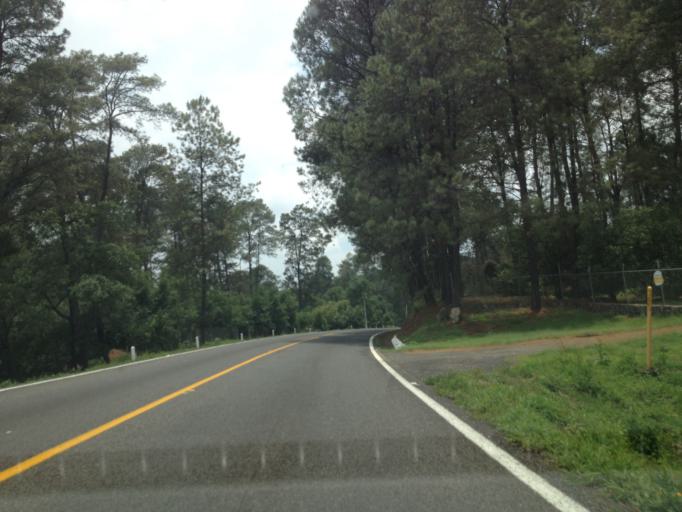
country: MX
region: Michoacan
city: Tingambato
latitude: 19.4760
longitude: -101.9235
